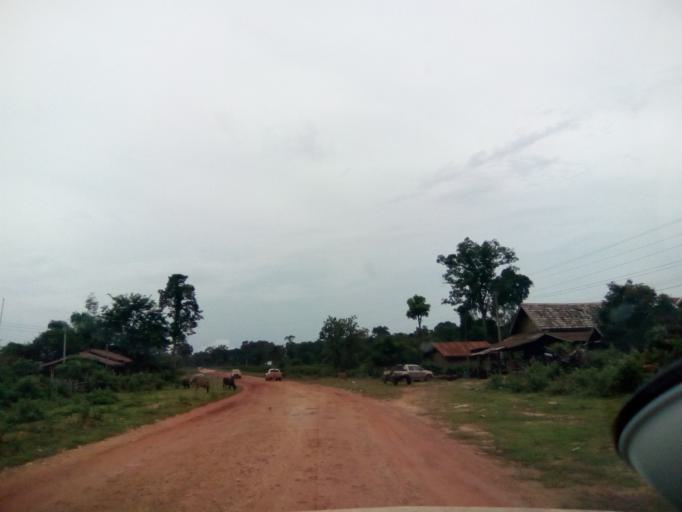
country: LA
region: Attapu
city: Attapu
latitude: 14.6756
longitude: 106.5692
